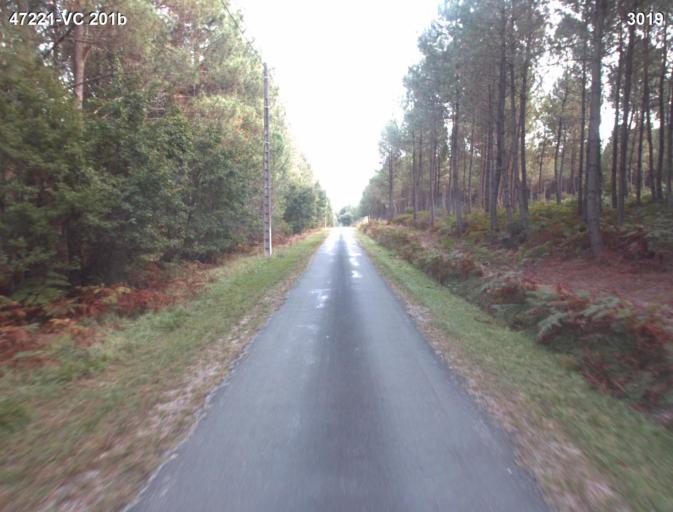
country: FR
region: Aquitaine
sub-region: Departement du Lot-et-Garonne
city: Mezin
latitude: 44.0862
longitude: 0.2165
